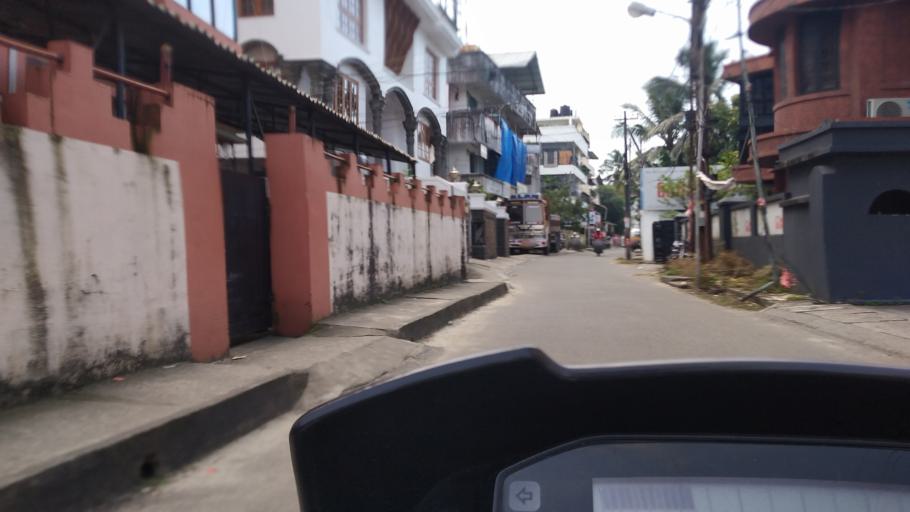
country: IN
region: Kerala
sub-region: Ernakulam
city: Cochin
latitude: 9.9780
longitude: 76.2867
